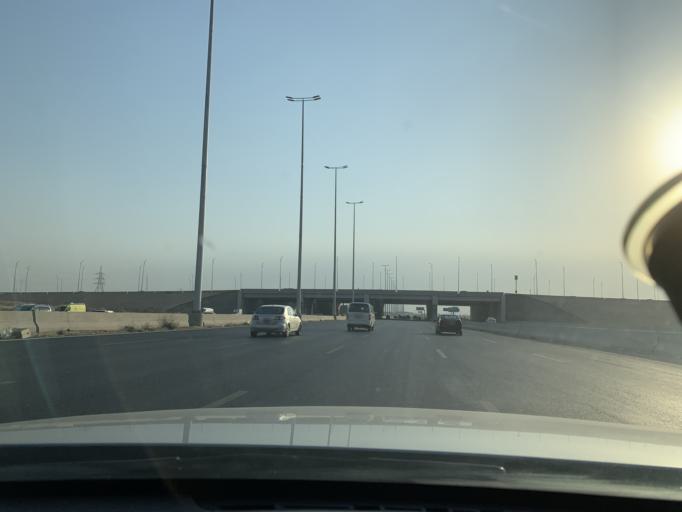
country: EG
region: Muhafazat al Qalyubiyah
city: Al Khankah
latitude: 30.1033
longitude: 31.5886
